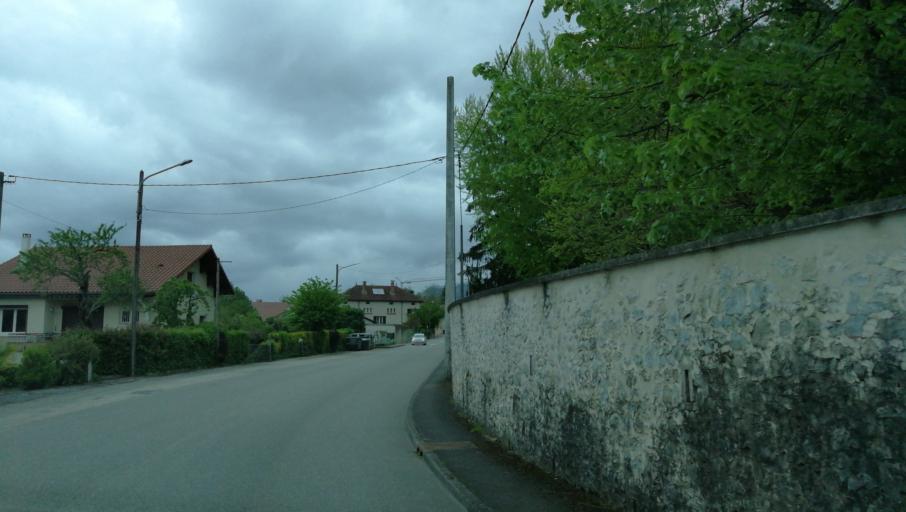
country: FR
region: Rhone-Alpes
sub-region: Departement de la Drome
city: Saint-Jean-en-Royans
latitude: 45.0126
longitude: 5.2886
